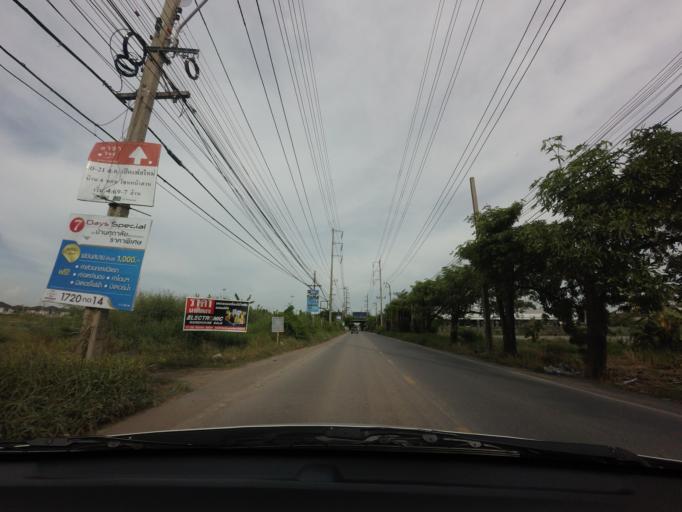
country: TH
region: Bangkok
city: Bang Na
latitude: 13.6187
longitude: 100.6603
